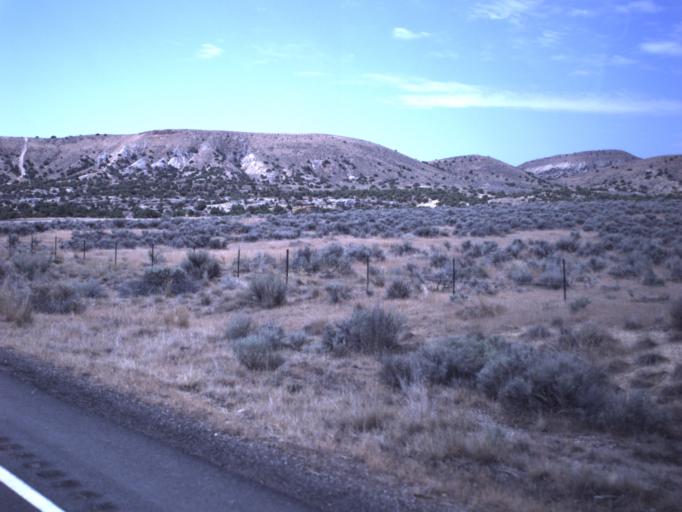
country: US
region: Utah
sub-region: Uintah County
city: Naples
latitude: 40.3584
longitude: -109.4982
